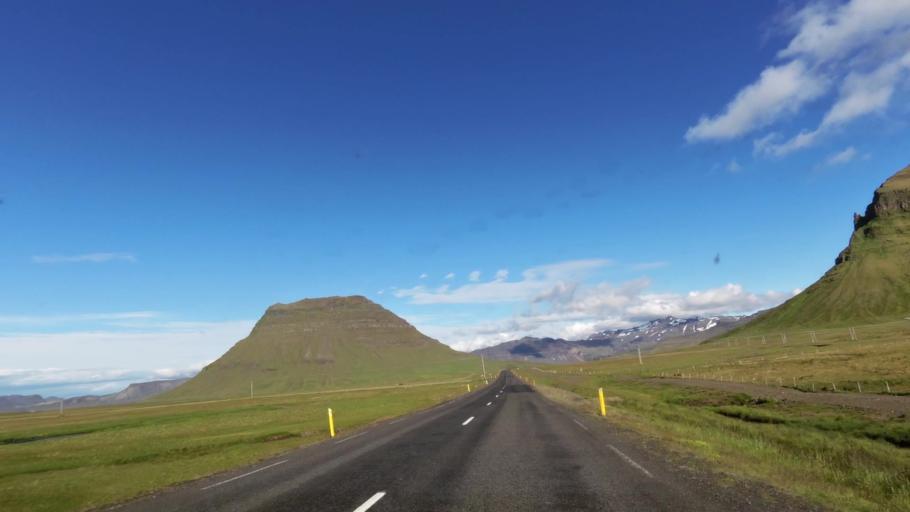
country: IS
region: West
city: Olafsvik
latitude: 64.9410
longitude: -23.3733
